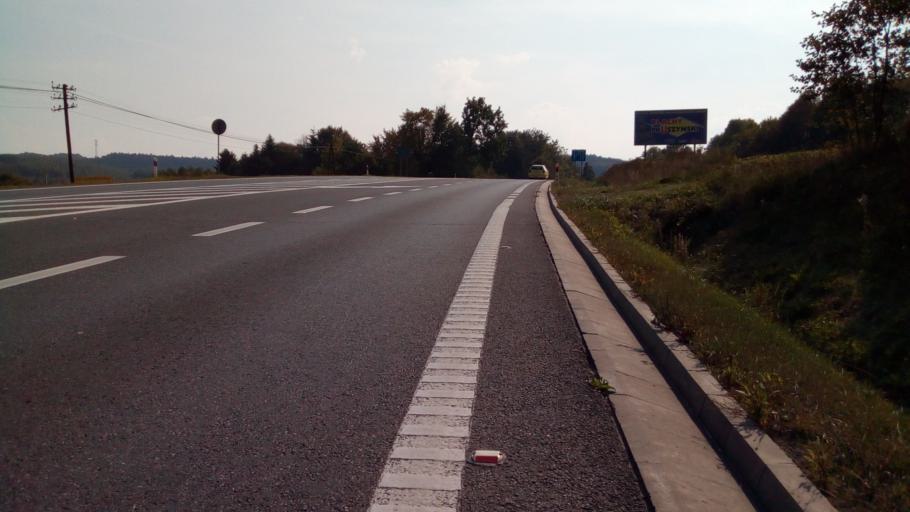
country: PL
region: Subcarpathian Voivodeship
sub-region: Powiat strzyzowski
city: Jawornik
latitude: 49.8379
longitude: 21.8883
